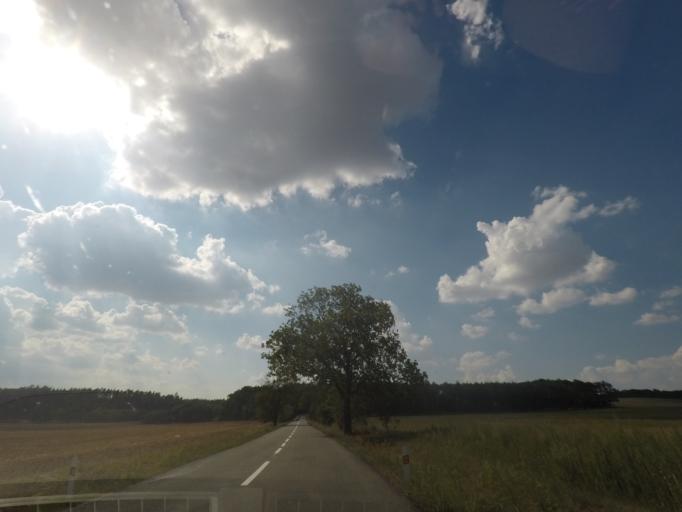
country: CZ
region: Kralovehradecky
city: Trebechovice pod Orebem
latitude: 50.2191
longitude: 15.9802
